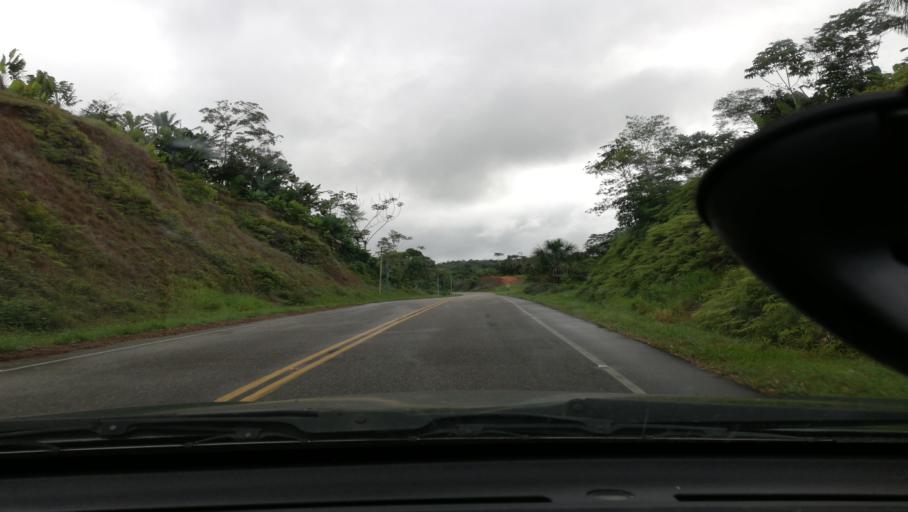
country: PE
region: Loreto
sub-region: Provincia de Loreto
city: Nauta
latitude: -4.4789
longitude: -73.5956
